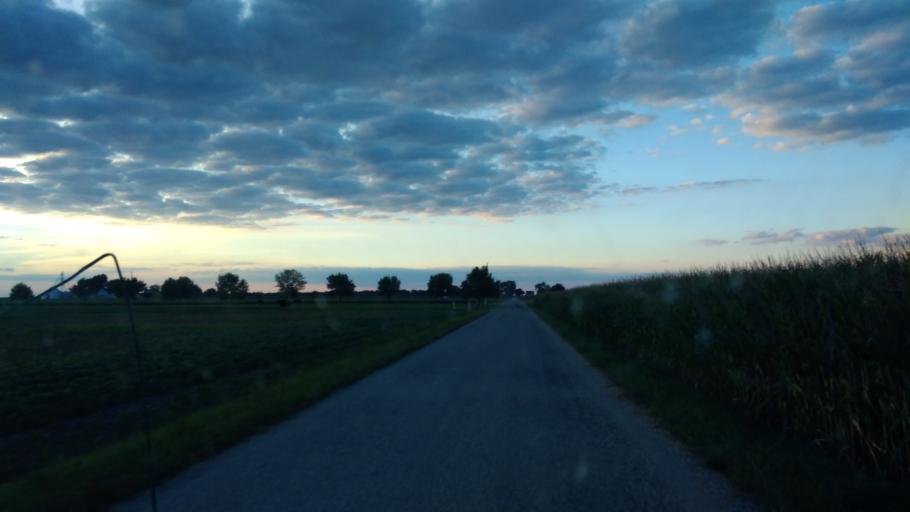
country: US
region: Indiana
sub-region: Adams County
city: Geneva
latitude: 40.6251
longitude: -85.0602
